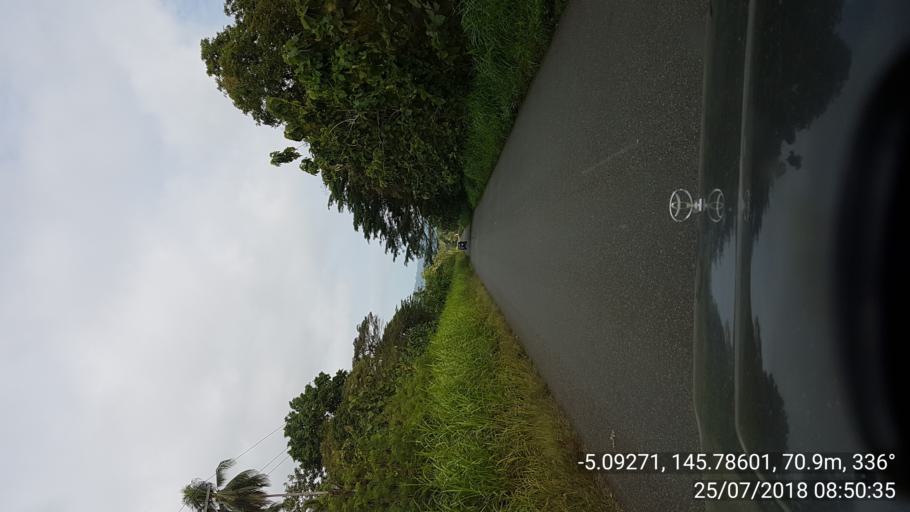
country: PG
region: Madang
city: Madang
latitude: -5.0928
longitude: 145.7861
